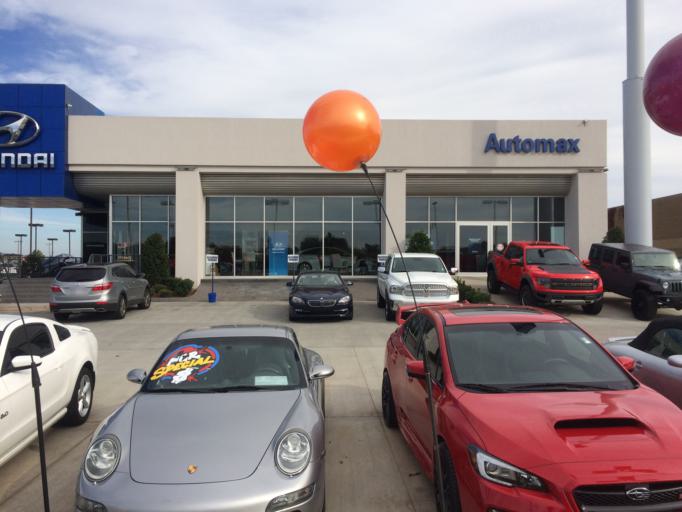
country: US
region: Oklahoma
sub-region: Cleveland County
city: Norman
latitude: 35.2245
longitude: -97.4850
